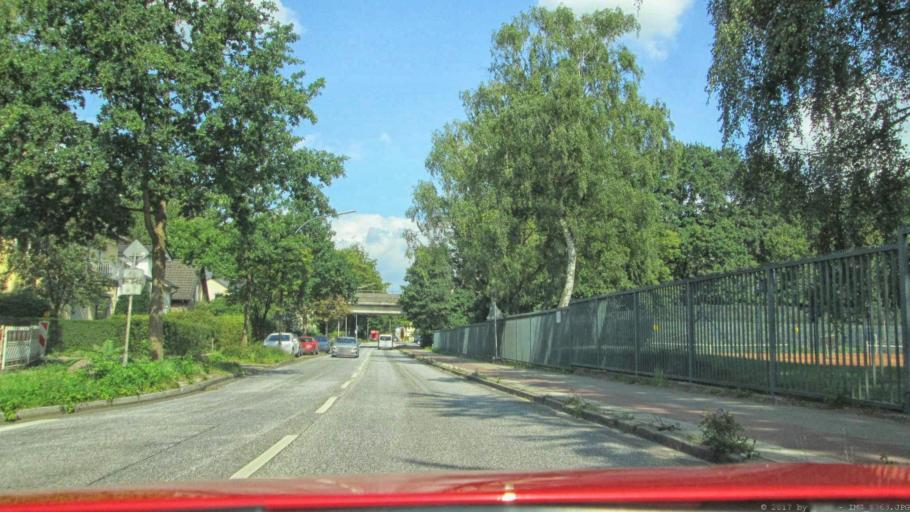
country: DE
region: Schleswig-Holstein
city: Halstenbek
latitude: 53.5644
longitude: 9.8265
